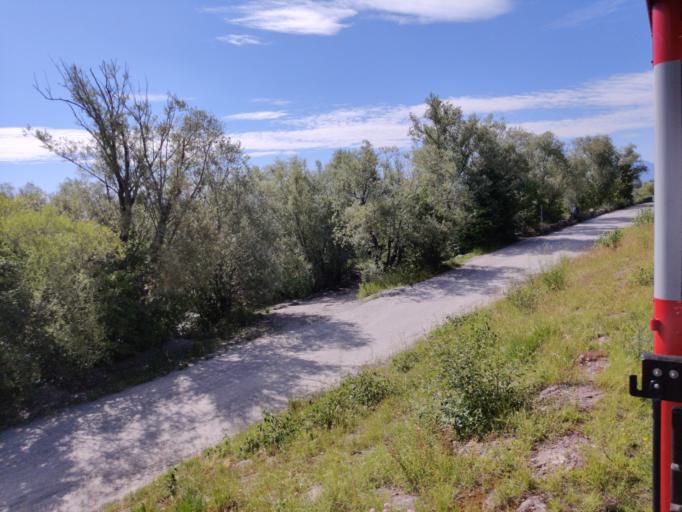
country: AT
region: Vorarlberg
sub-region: Politischer Bezirk Bregenz
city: Hard
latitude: 47.4992
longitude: 9.6720
